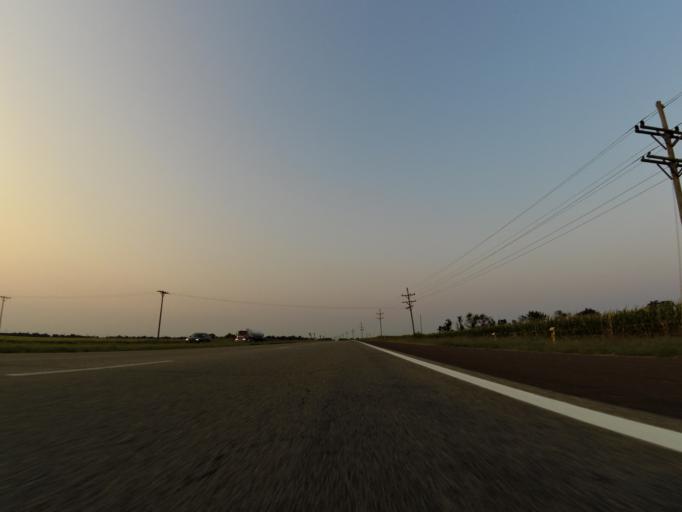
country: US
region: Kansas
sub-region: Reno County
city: South Hutchinson
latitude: 38.0007
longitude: -97.9406
